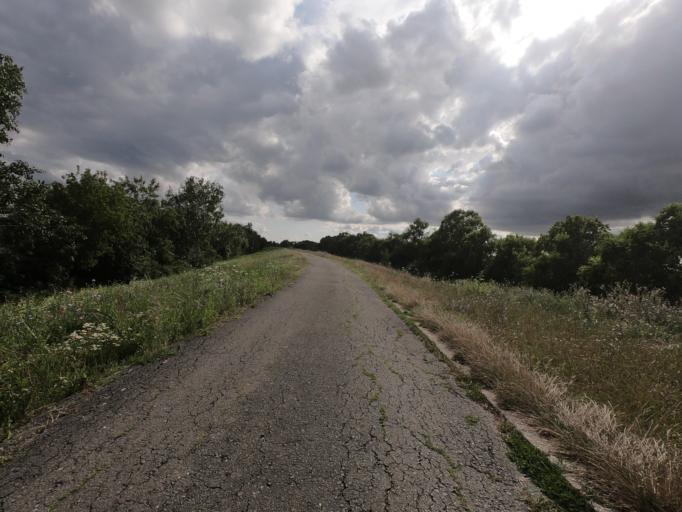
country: HU
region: Heves
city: Poroszlo
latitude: 47.6642
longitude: 20.6883
